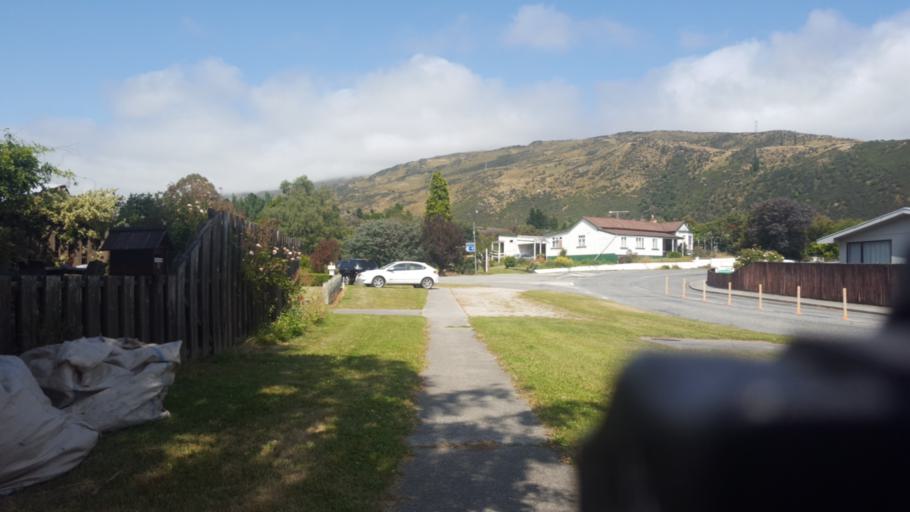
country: NZ
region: Otago
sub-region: Queenstown-Lakes District
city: Kingston
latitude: -45.5428
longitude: 169.3202
